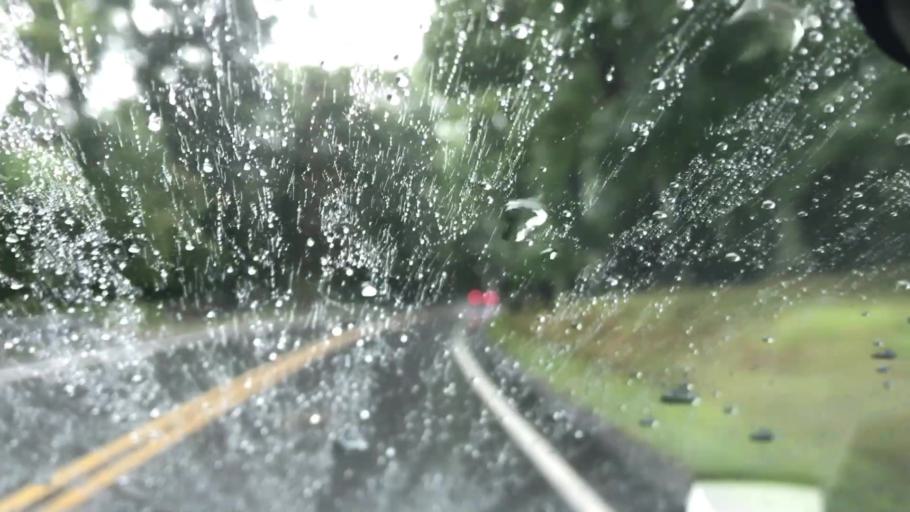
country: US
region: Pennsylvania
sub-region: Allegheny County
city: Allison Park
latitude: 40.5582
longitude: -79.9850
